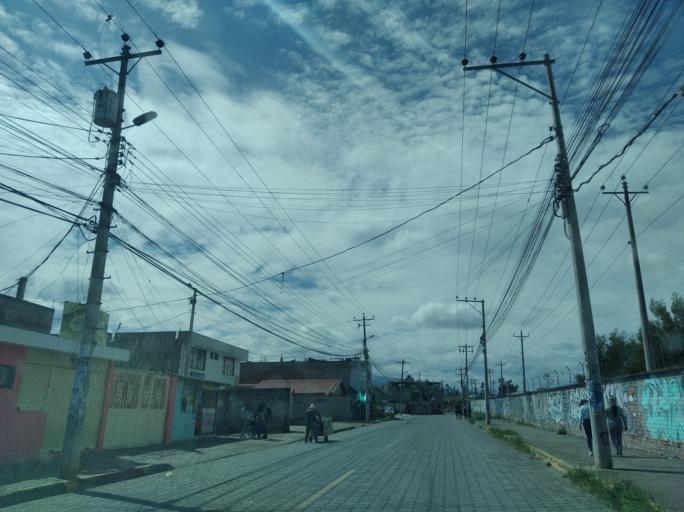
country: EC
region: Pichincha
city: Sangolqui
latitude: -0.2153
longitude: -78.3398
